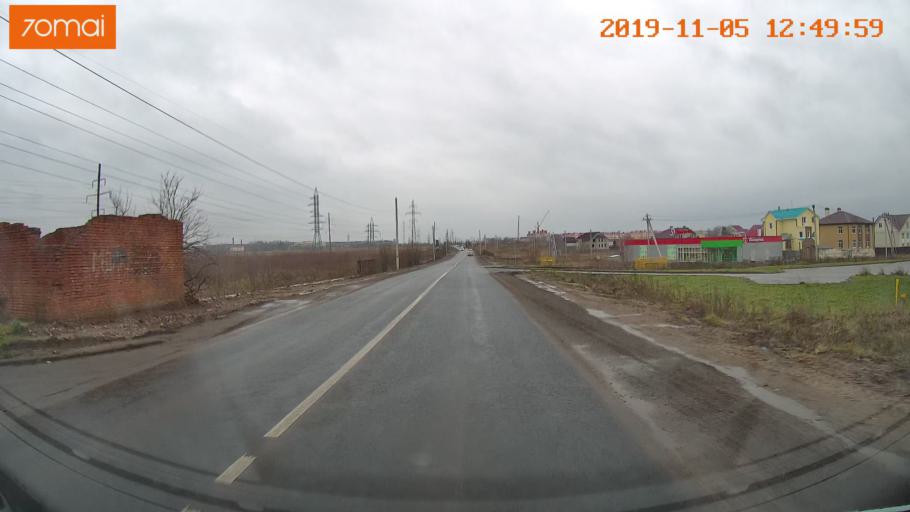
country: RU
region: Ivanovo
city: Kokhma
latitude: 56.9511
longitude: 41.1072
